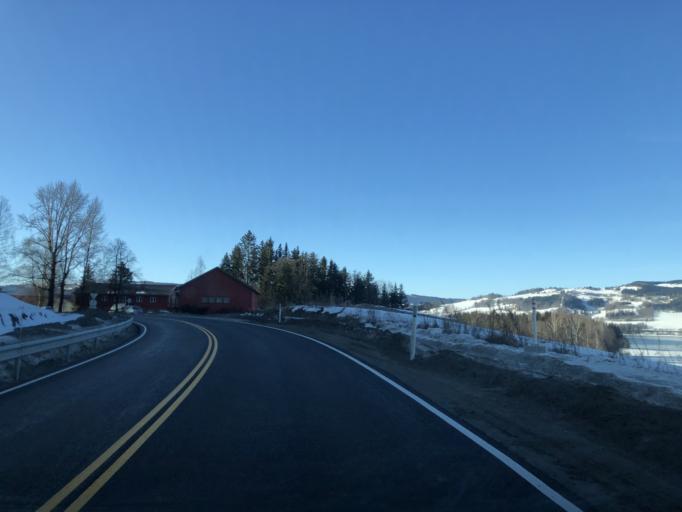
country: NO
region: Hedmark
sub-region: Ringsaker
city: Moelv
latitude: 60.9106
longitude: 10.7061
